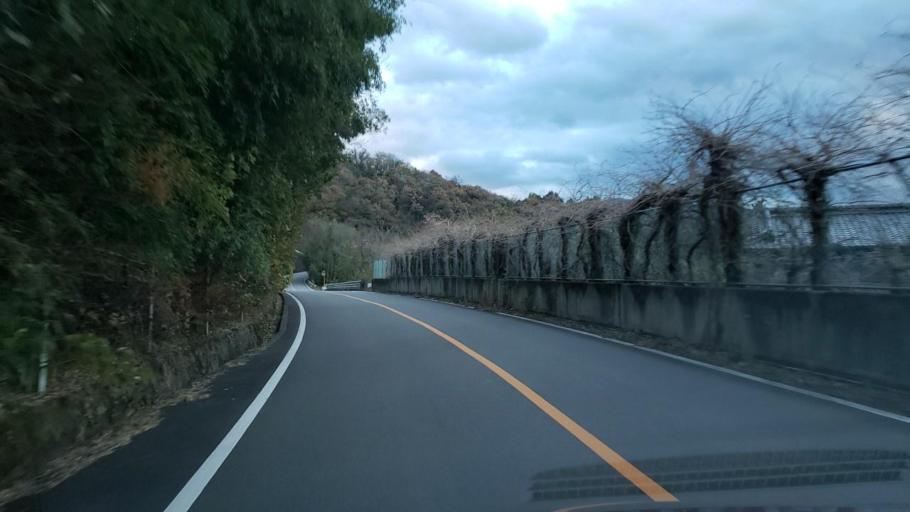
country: JP
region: Tokushima
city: Wakimachi
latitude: 34.0892
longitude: 134.1780
